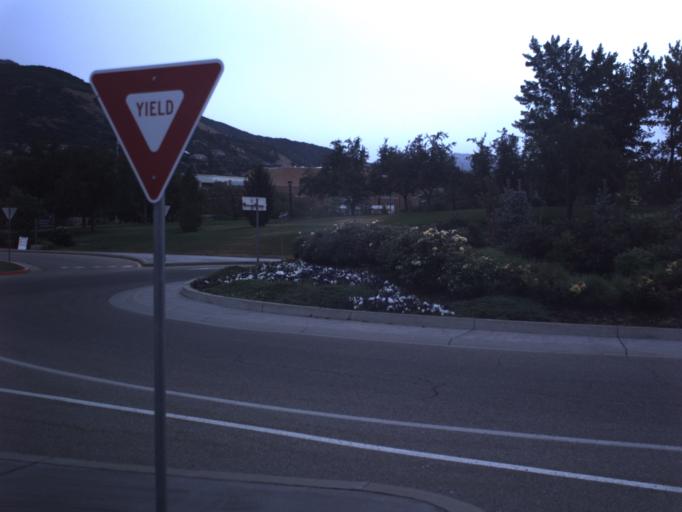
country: US
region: Utah
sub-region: Weber County
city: South Ogden
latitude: 41.1936
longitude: -111.9479
